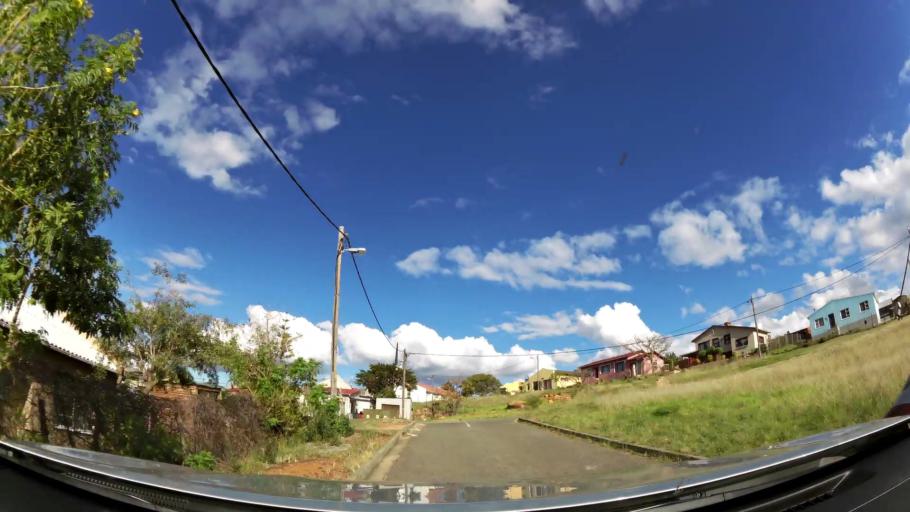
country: ZA
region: Western Cape
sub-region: Overberg District Municipality
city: Swellendam
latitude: -34.0331
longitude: 20.4411
